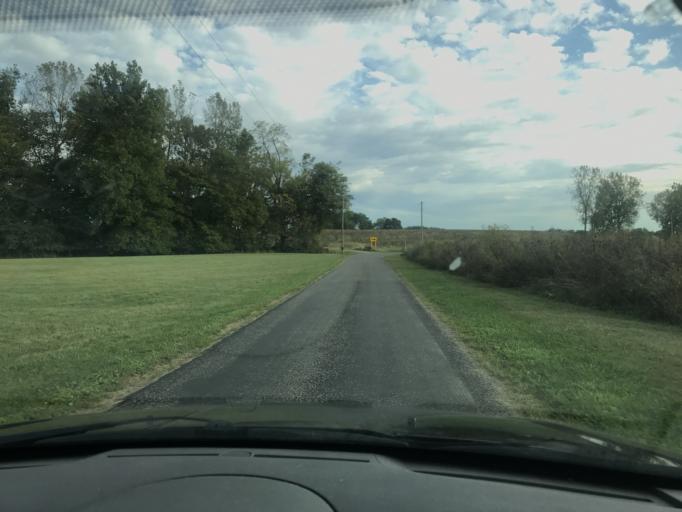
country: US
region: Ohio
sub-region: Logan County
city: West Liberty
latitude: 40.2207
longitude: -83.6752
